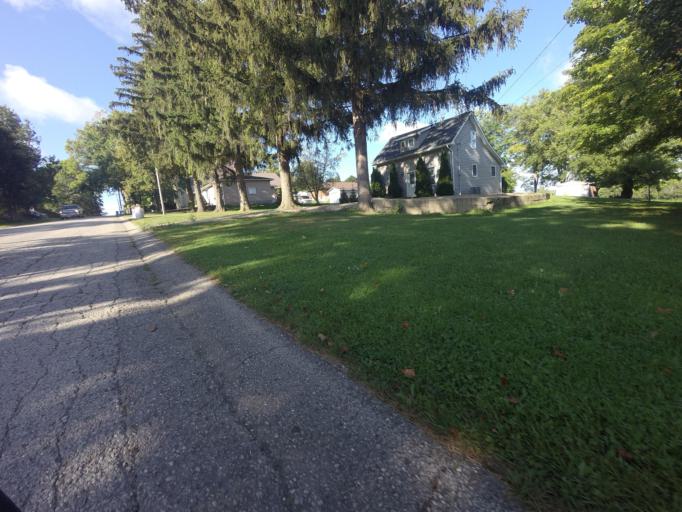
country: CA
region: Ontario
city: Huron East
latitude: 43.7379
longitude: -81.4306
